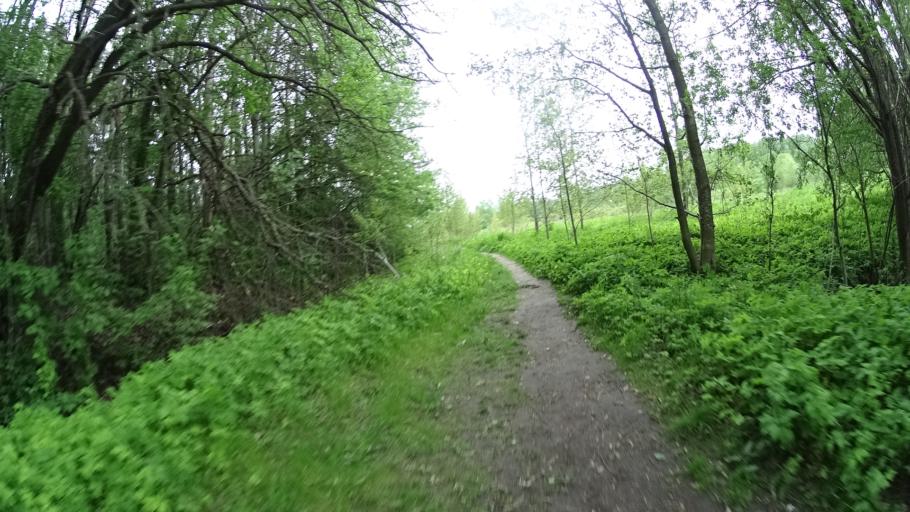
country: FI
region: Uusimaa
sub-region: Helsinki
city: Vantaa
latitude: 60.2779
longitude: 25.0579
